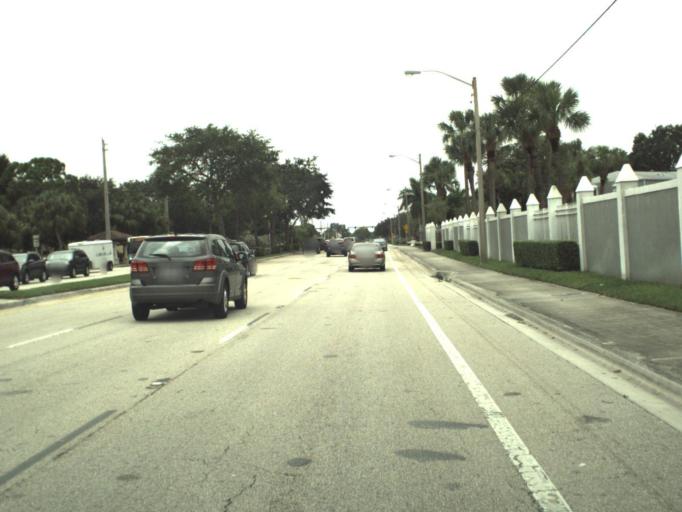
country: US
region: Florida
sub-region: Palm Beach County
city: North Palm Beach
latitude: 26.8304
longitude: -80.1056
